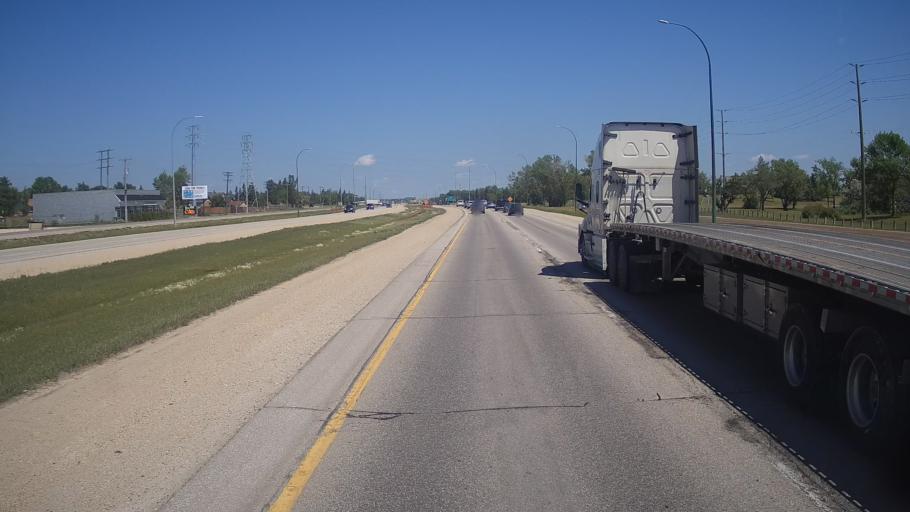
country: CA
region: Manitoba
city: Winnipeg
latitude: 49.9340
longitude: -97.0417
